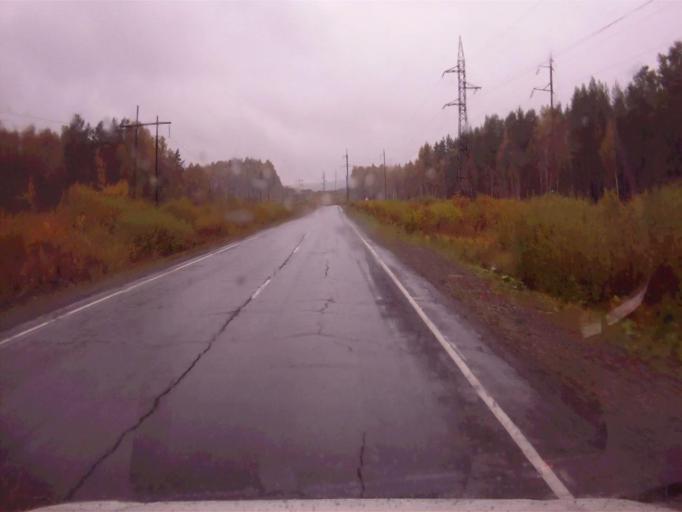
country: RU
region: Chelyabinsk
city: Verkhniy Ufaley
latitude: 55.9471
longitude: 60.4041
